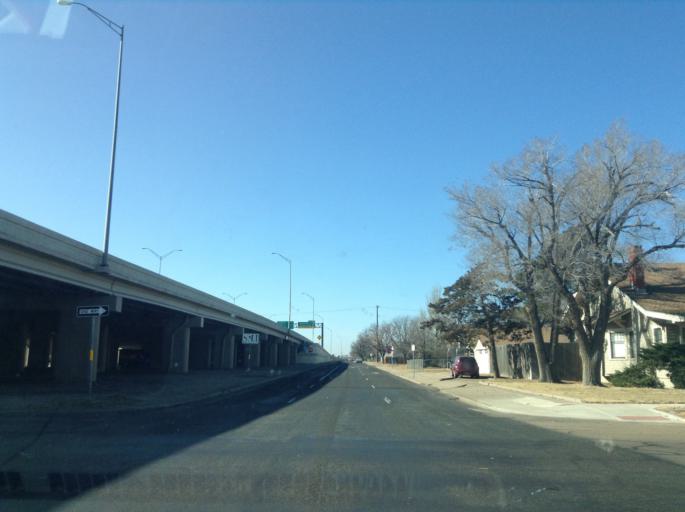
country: US
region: Texas
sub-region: Potter County
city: Amarillo
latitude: 35.1939
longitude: -101.8411
